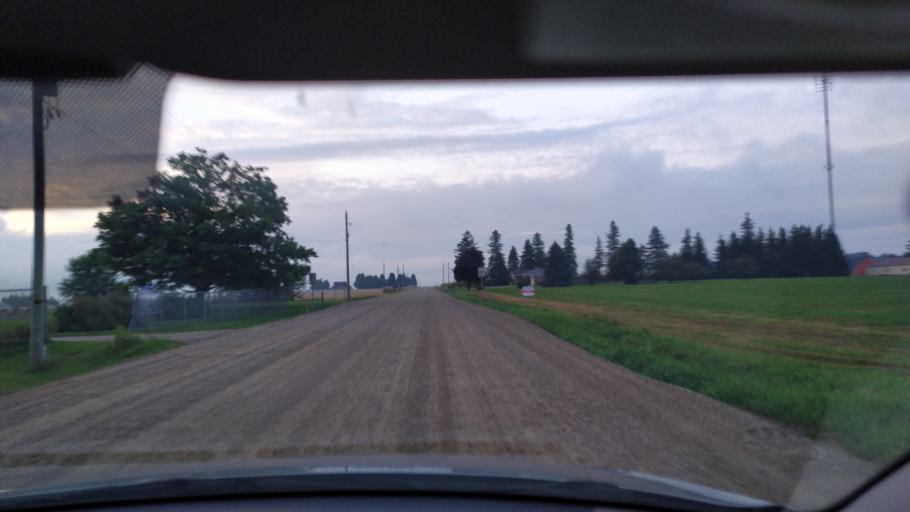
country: CA
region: Ontario
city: Kitchener
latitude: 43.3111
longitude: -80.6117
